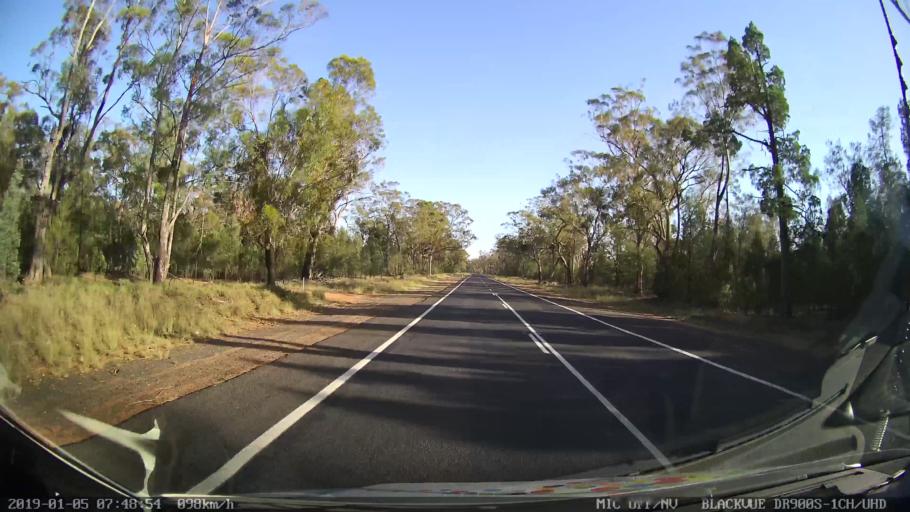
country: AU
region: New South Wales
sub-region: Gilgandra
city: Gilgandra
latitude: -31.8096
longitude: 148.6364
